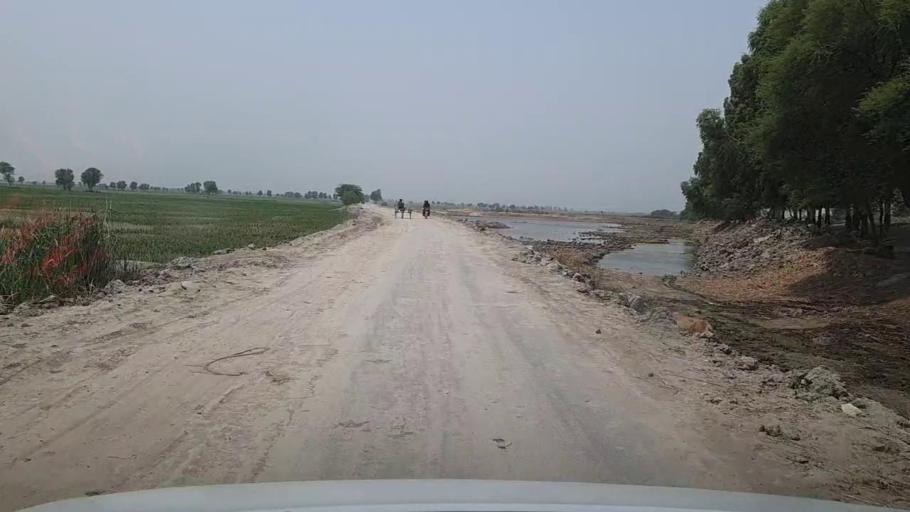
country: PK
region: Sindh
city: Sita Road
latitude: 27.0917
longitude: 67.9146
